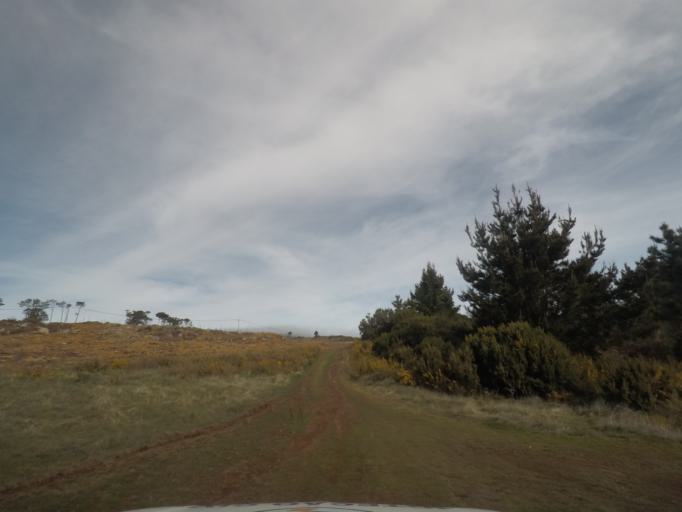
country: PT
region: Madeira
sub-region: Funchal
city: Nossa Senhora do Monte
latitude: 32.7123
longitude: -16.9077
